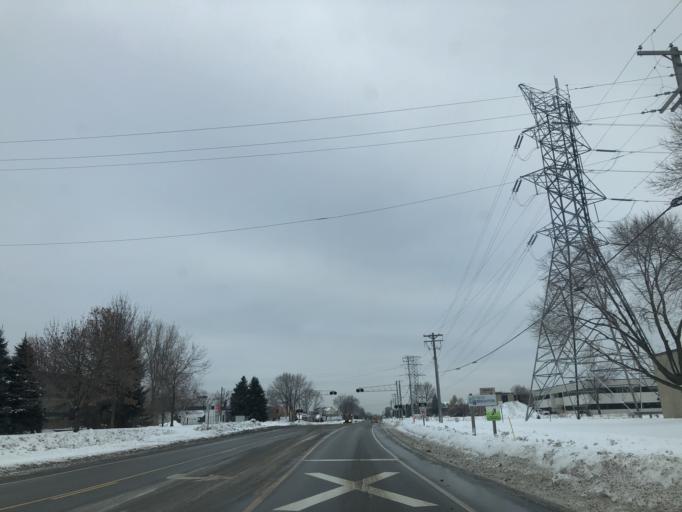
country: US
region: Minnesota
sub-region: Ramsey County
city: New Brighton
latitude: 45.0862
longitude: -93.1884
